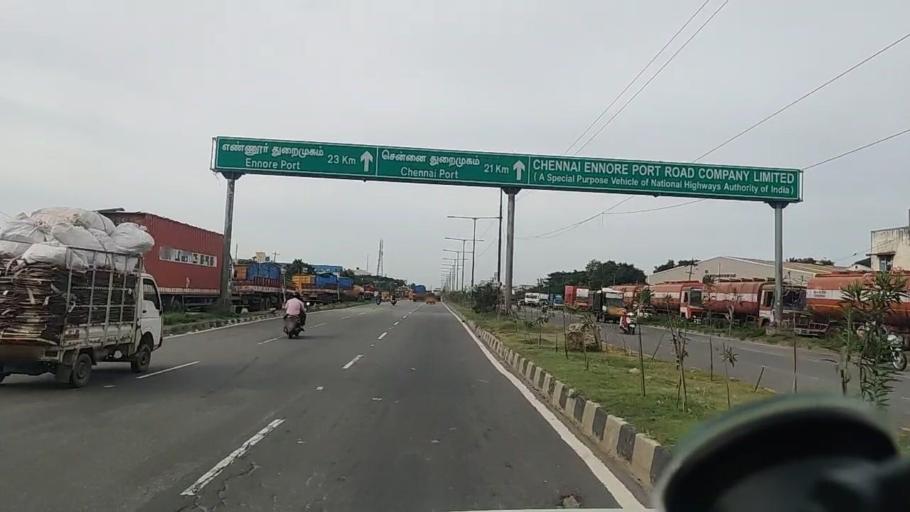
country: IN
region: Tamil Nadu
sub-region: Thiruvallur
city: Chinnasekkadu
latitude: 13.1508
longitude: 80.2227
